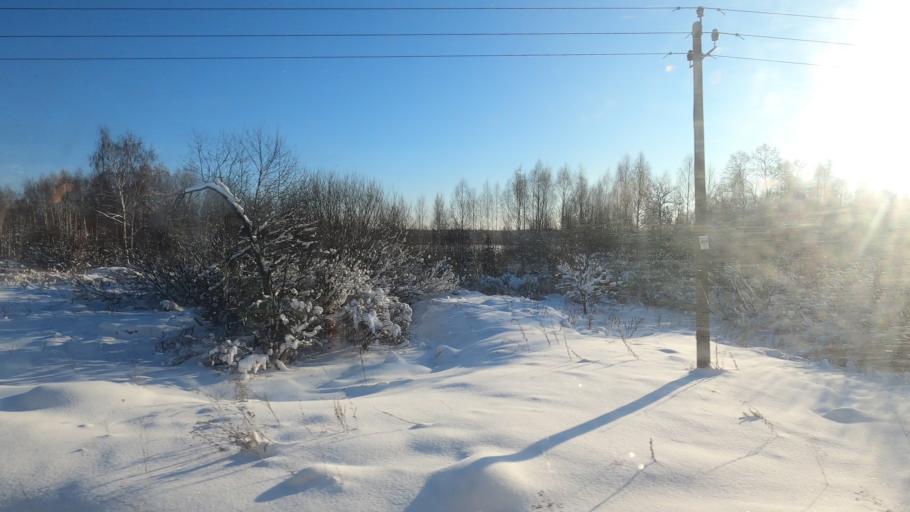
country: RU
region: Moskovskaya
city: Zhukovka
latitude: 56.4717
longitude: 37.5337
